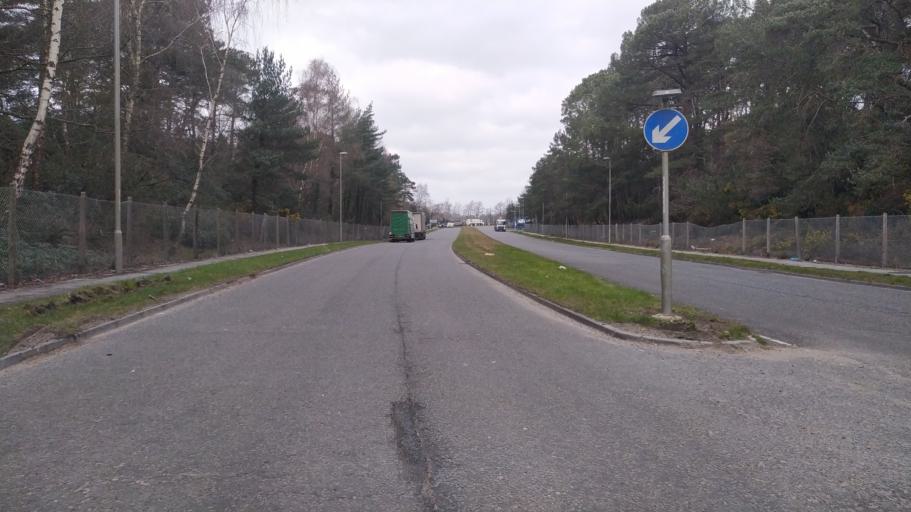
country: GB
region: England
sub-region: Dorset
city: Lytchett Matravers
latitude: 50.7202
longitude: -2.0772
